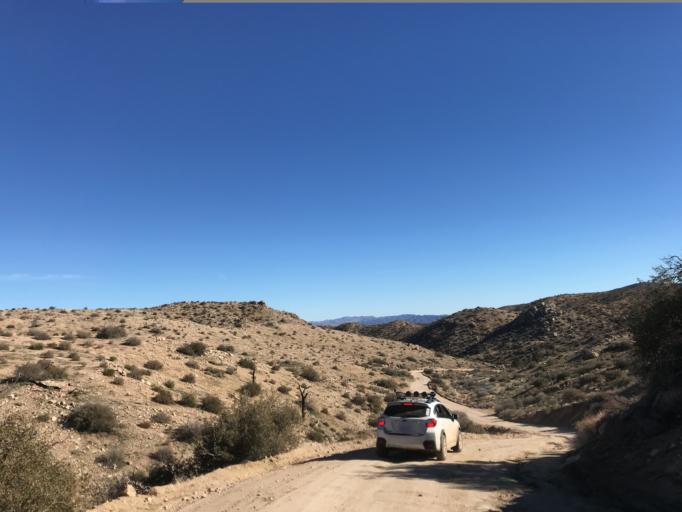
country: US
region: California
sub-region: San Bernardino County
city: Morongo Valley
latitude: 34.2090
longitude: -116.6020
